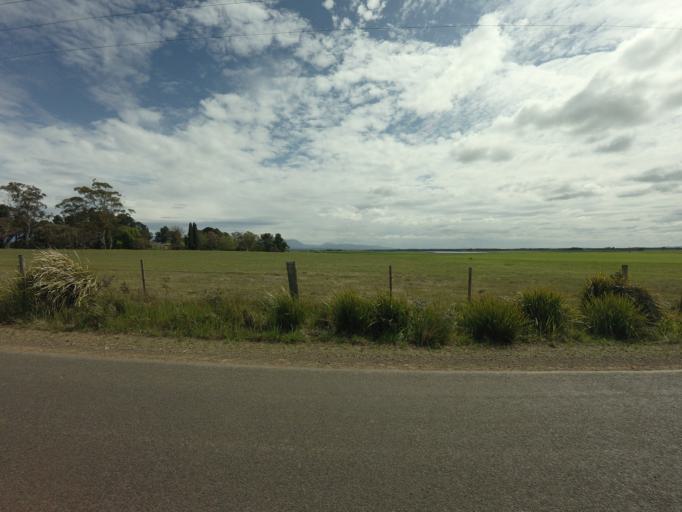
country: AU
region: Tasmania
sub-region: Northern Midlands
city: Longford
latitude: -41.7120
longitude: 147.1951
